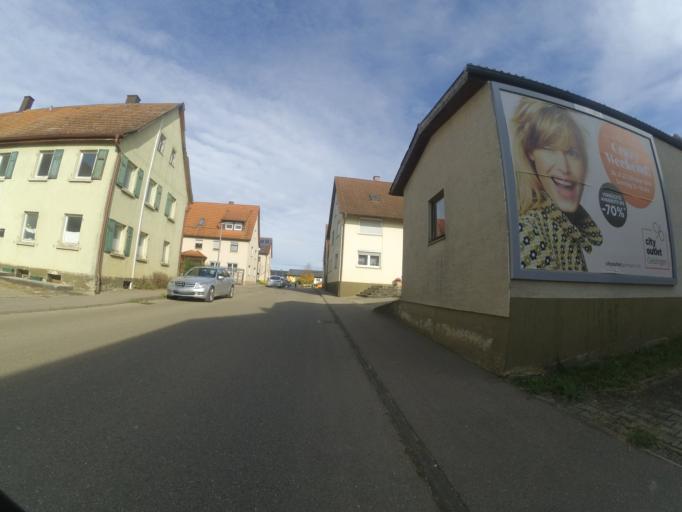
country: DE
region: Baden-Wuerttemberg
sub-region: Tuebingen Region
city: Lonsee
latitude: 48.5646
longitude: 9.9246
